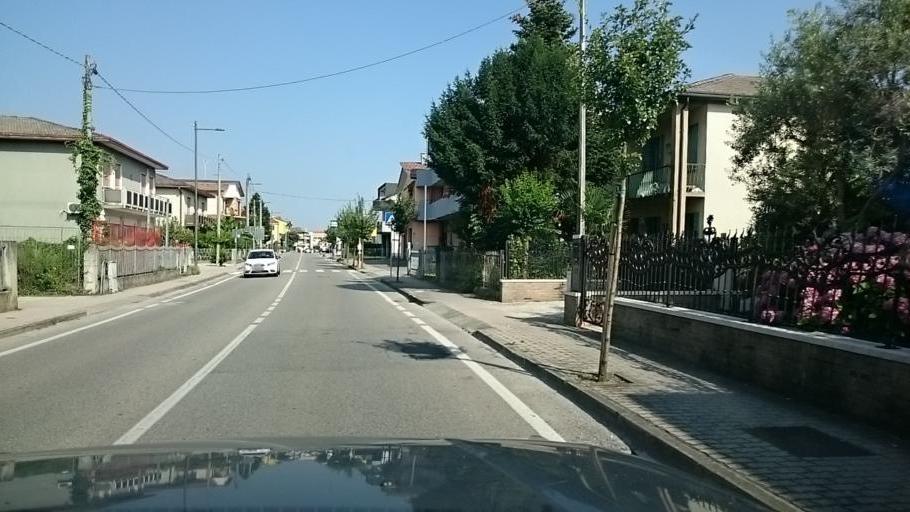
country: IT
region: Veneto
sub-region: Provincia di Padova
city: Vigodarzere
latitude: 45.4541
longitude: 11.8840
